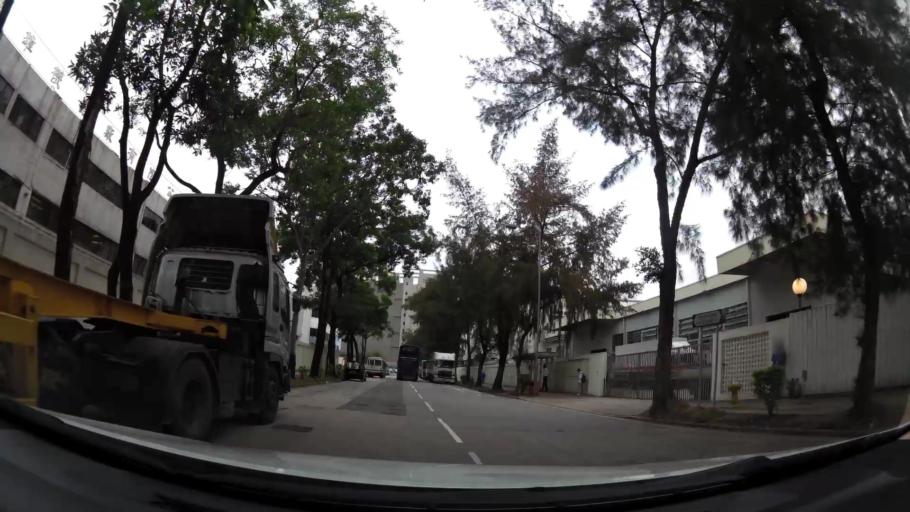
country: HK
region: Tai Po
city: Tai Po
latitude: 22.4582
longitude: 114.1833
